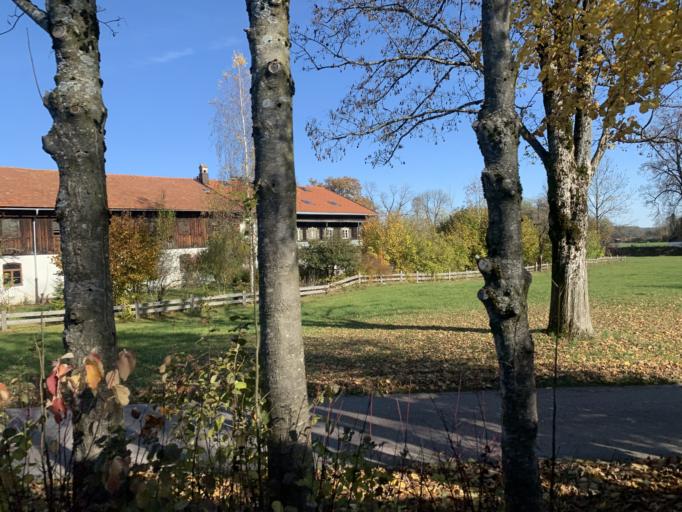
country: DE
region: Bavaria
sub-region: Upper Bavaria
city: Gmund am Tegernsee
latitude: 47.7754
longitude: 11.7122
